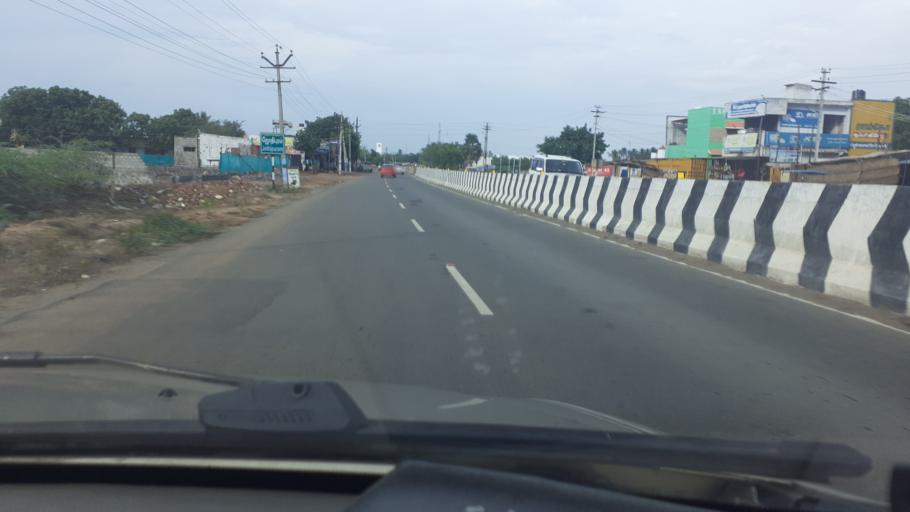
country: IN
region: Tamil Nadu
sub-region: Tirunelveli Kattabo
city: Tirunelveli
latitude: 8.6649
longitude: 77.7162
